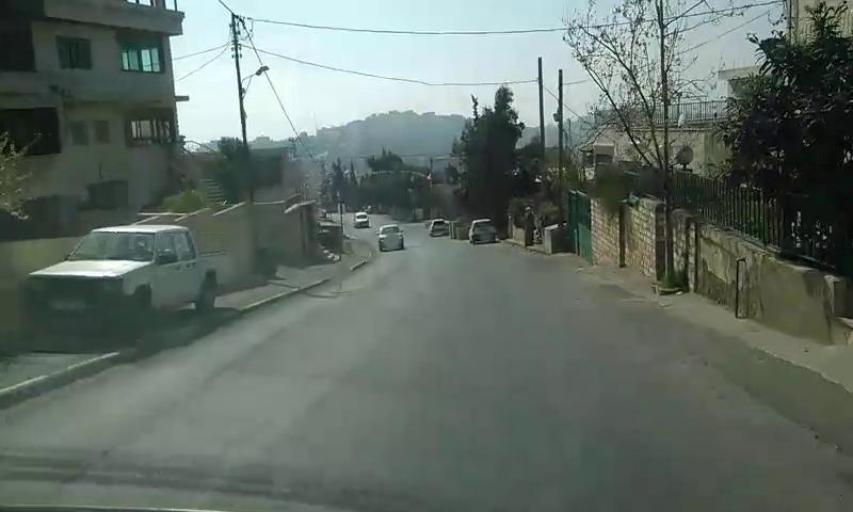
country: PS
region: West Bank
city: Dayr Jarir
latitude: 31.9635
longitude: 35.2941
